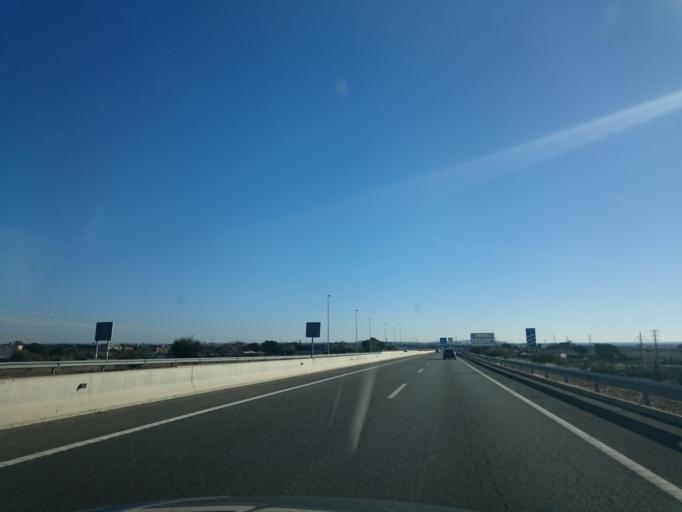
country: ES
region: Catalonia
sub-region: Provincia de Tarragona
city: Cambrils
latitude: 41.0844
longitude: 1.0638
